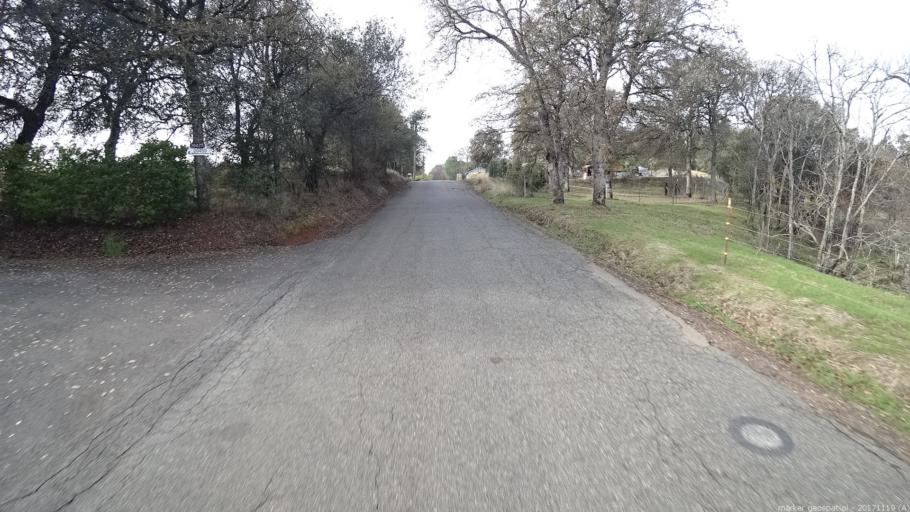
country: US
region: California
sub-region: Shasta County
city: Anderson
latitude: 40.4766
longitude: -122.2954
